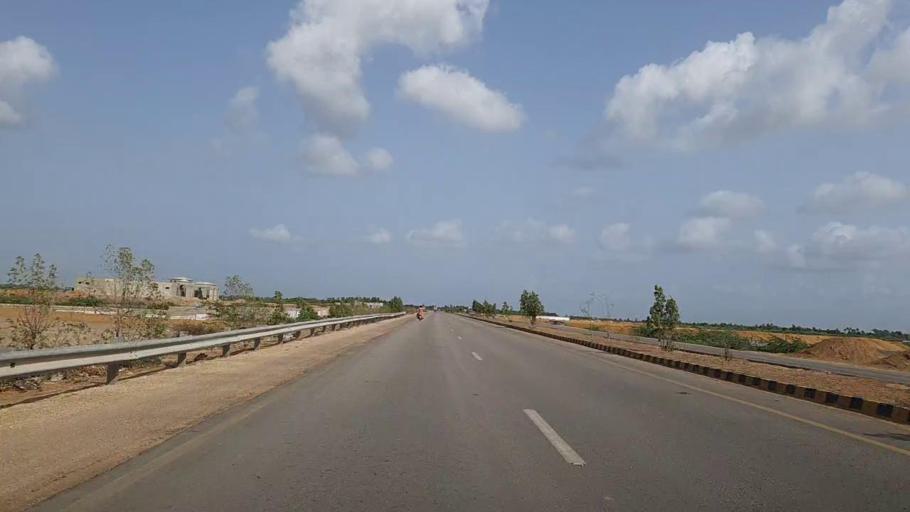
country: PK
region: Sindh
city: Gharo
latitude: 24.7352
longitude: 67.6003
